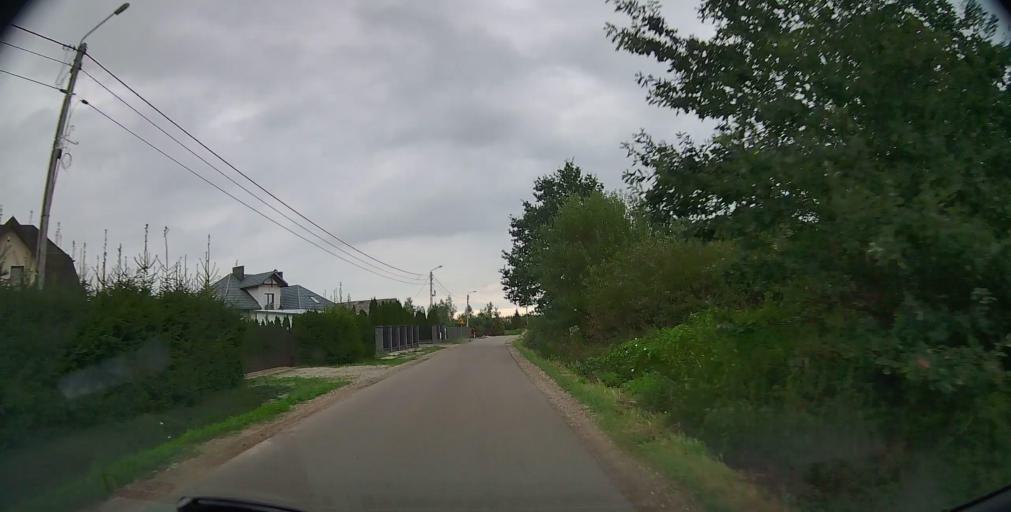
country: PL
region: Masovian Voivodeship
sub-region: Powiat radomski
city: Jedlinsk
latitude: 51.4509
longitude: 21.0958
